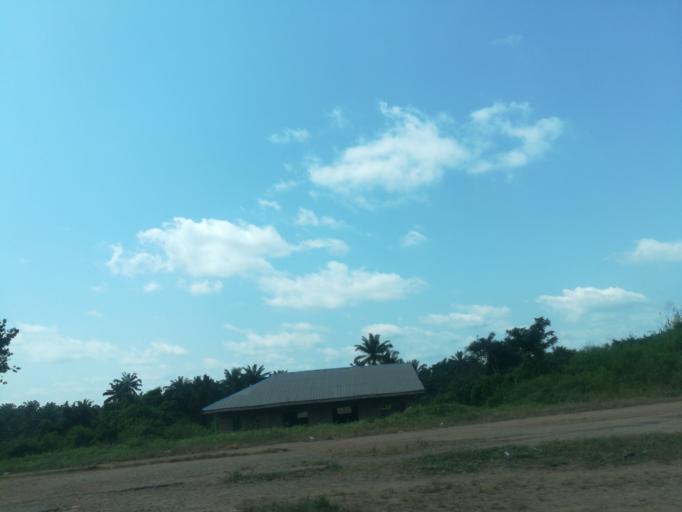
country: NG
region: Oyo
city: Moniya
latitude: 7.5854
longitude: 3.9114
